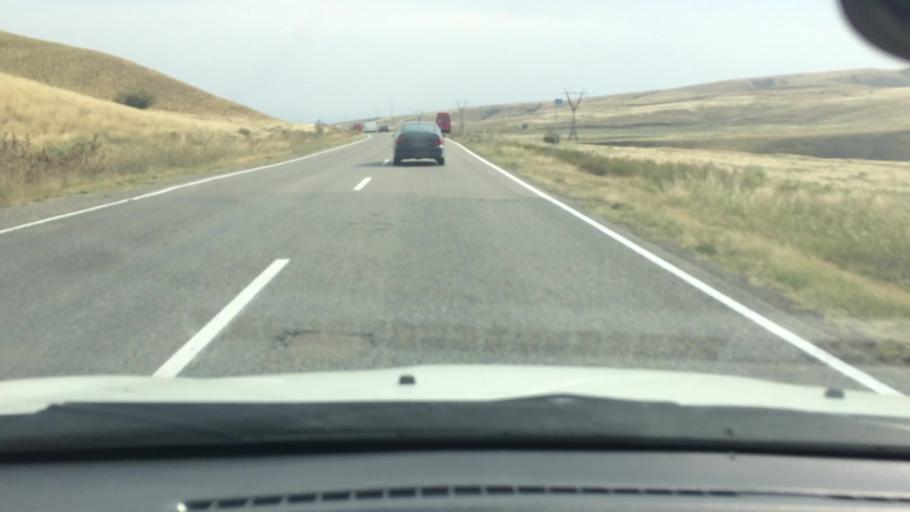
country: GE
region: Kvemo Kartli
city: Rust'avi
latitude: 41.5034
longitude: 44.9545
